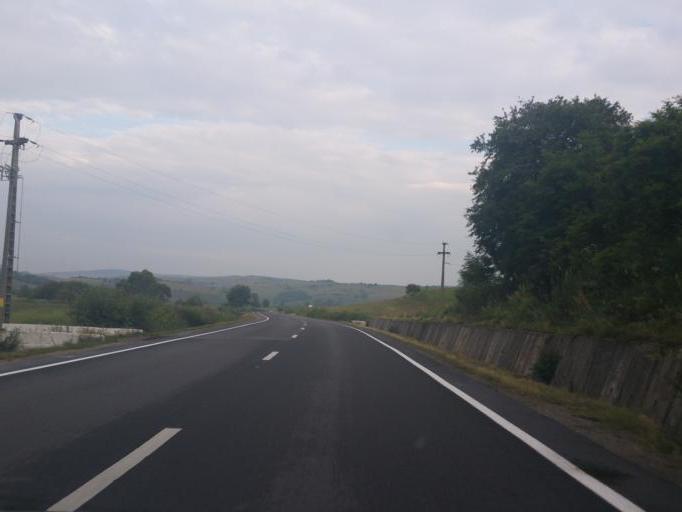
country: RO
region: Cluj
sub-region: Comuna Sanpaul
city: Sanpaul
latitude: 46.8892
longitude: 23.4124
